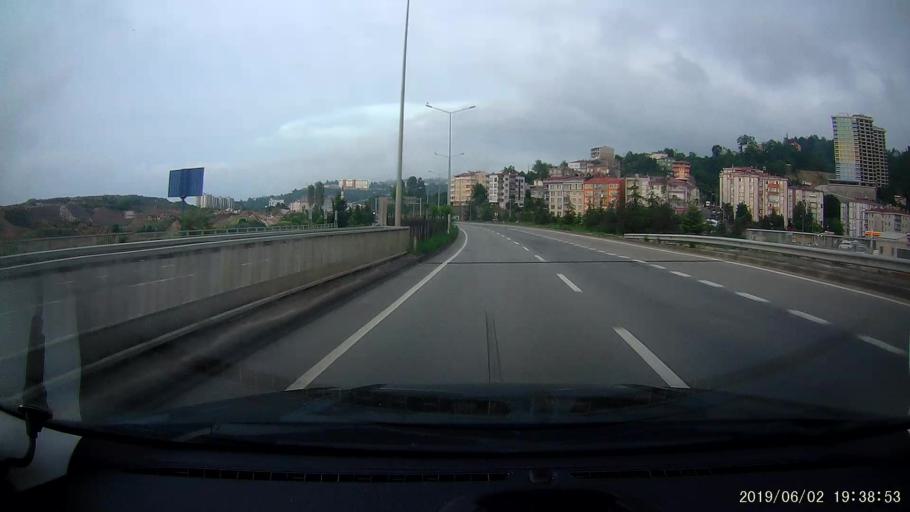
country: TR
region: Giresun
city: Giresun
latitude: 40.9119
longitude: 38.4300
